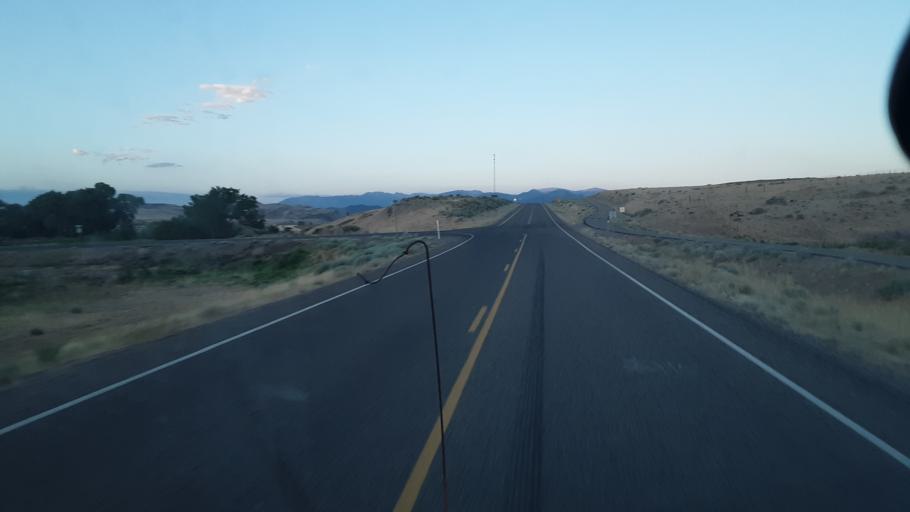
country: US
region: Utah
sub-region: Sevier County
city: Monroe
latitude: 38.6632
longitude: -112.1735
